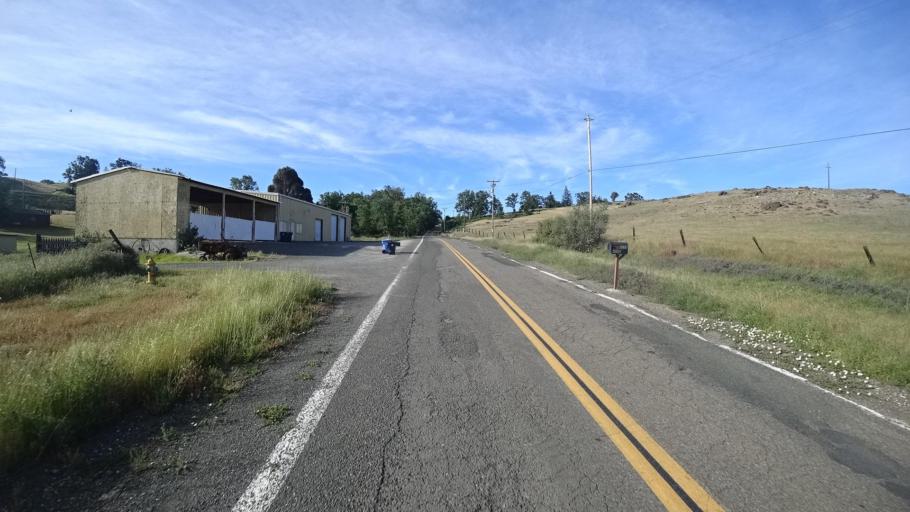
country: US
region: California
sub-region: Lake County
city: North Lakeport
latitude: 39.0936
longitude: -122.9176
